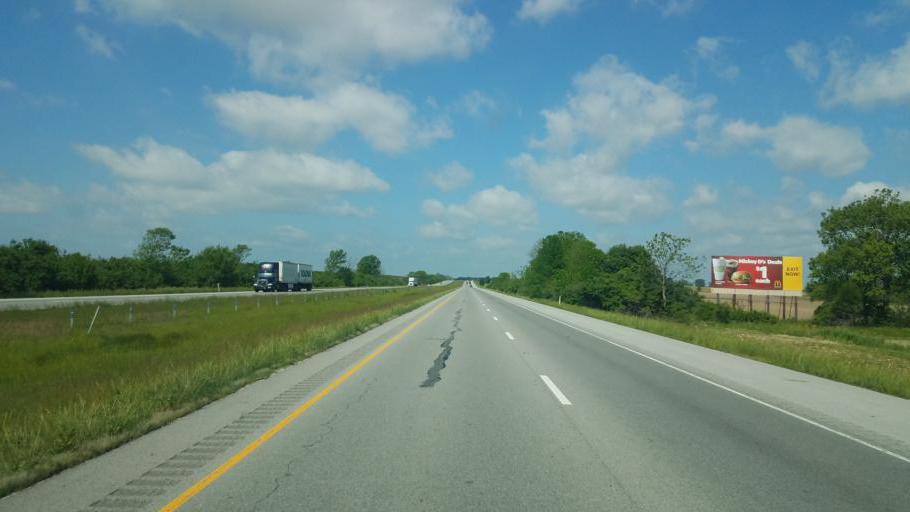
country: US
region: Indiana
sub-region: Putnam County
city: Cloverdale
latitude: 39.5560
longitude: -86.6839
